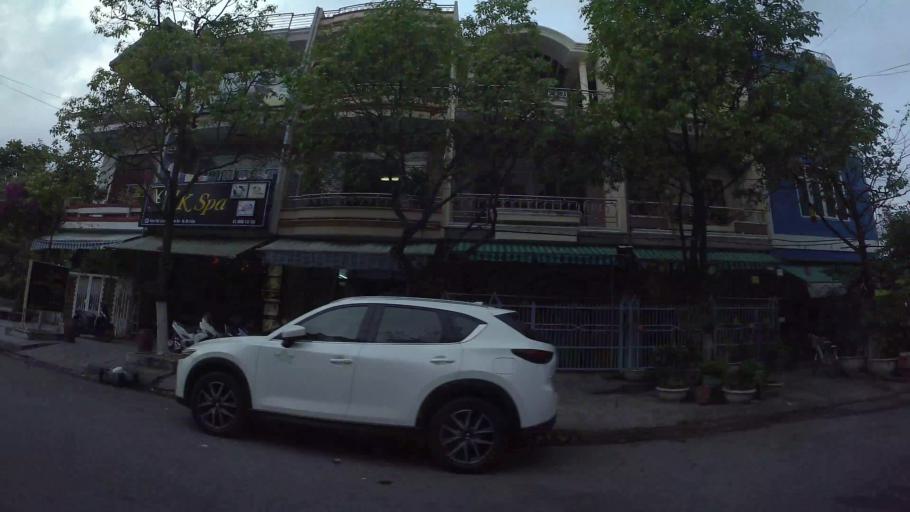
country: VN
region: Da Nang
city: Son Tra
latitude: 16.0650
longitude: 108.2326
